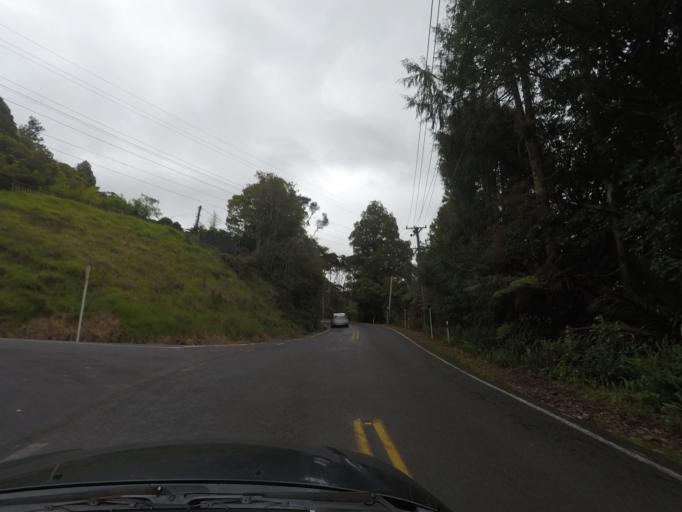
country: NZ
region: Auckland
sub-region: Auckland
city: Titirangi
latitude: -36.9325
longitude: 174.5881
